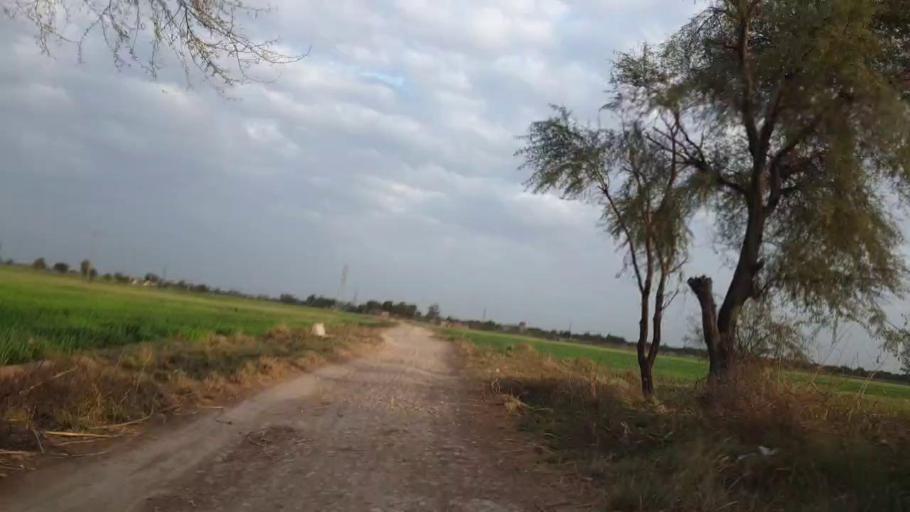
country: PK
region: Sindh
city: Matiari
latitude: 25.5683
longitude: 68.4425
